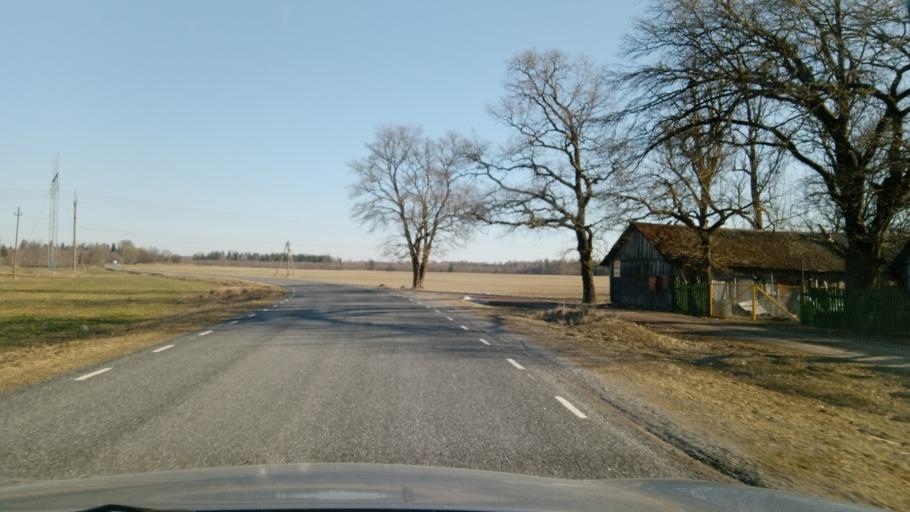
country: EE
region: Laeaene-Virumaa
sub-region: Tamsalu vald
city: Tamsalu
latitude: 59.1778
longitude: 26.1269
